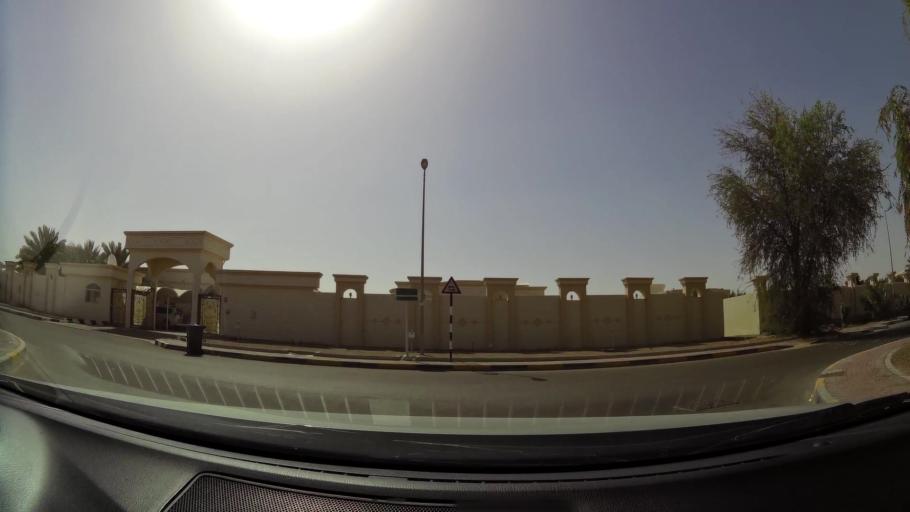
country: OM
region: Al Buraimi
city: Al Buraymi
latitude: 24.3049
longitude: 55.8012
